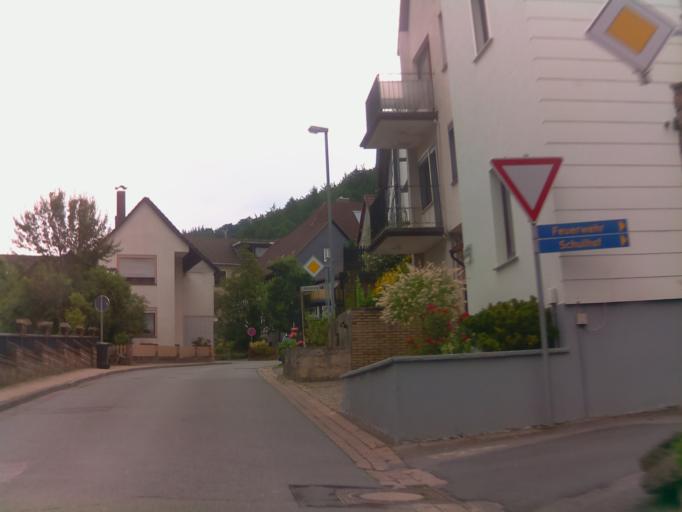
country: DE
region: Lower Saxony
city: Pegestorf
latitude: 51.9302
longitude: 9.5100
